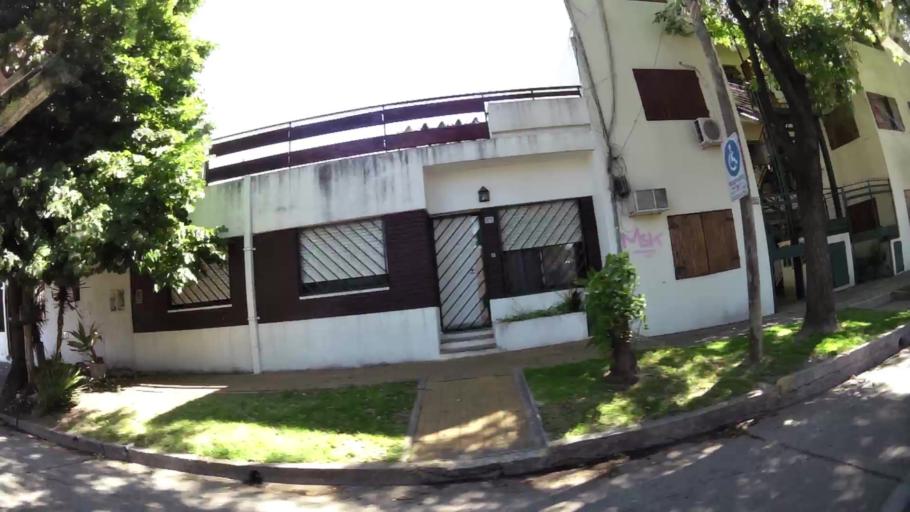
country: AR
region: Buenos Aires
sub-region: Partido de General San Martin
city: General San Martin
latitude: -34.5560
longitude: -58.5643
